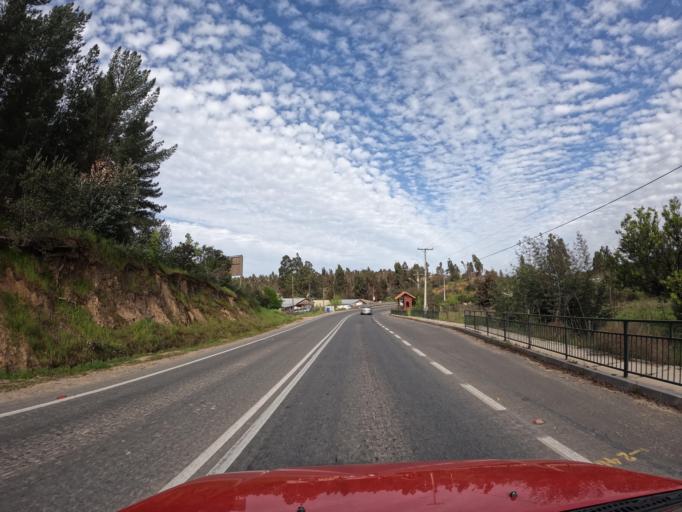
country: CL
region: O'Higgins
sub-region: Provincia de Colchagua
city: Santa Cruz
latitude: -34.3165
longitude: -71.7638
